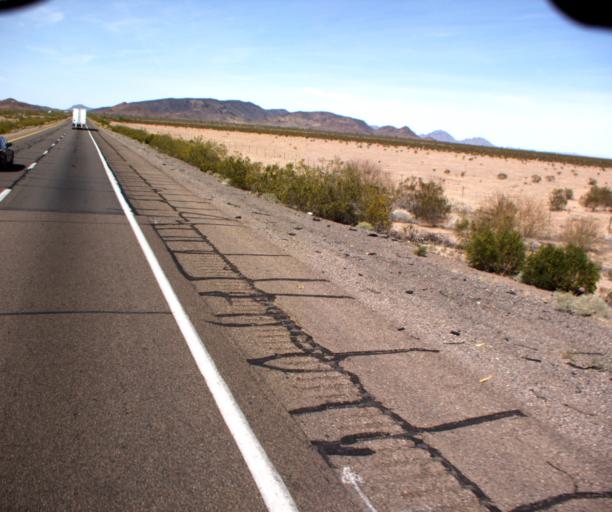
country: US
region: Arizona
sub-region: La Paz County
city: Salome
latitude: 33.6408
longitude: -113.8350
